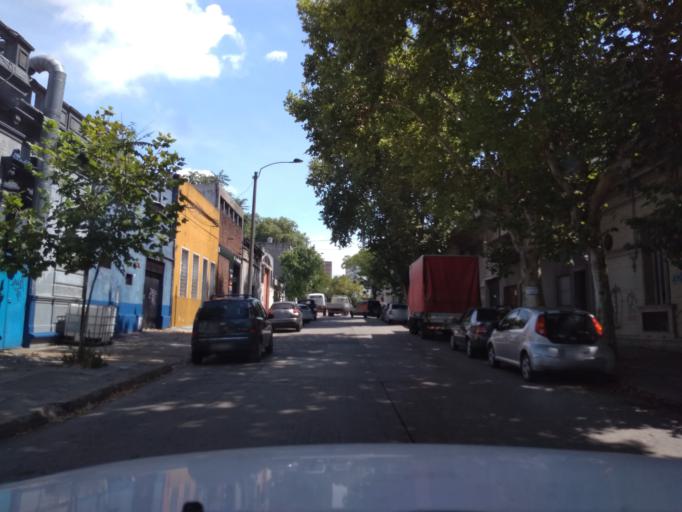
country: UY
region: Montevideo
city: Montevideo
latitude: -34.8797
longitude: -56.1971
